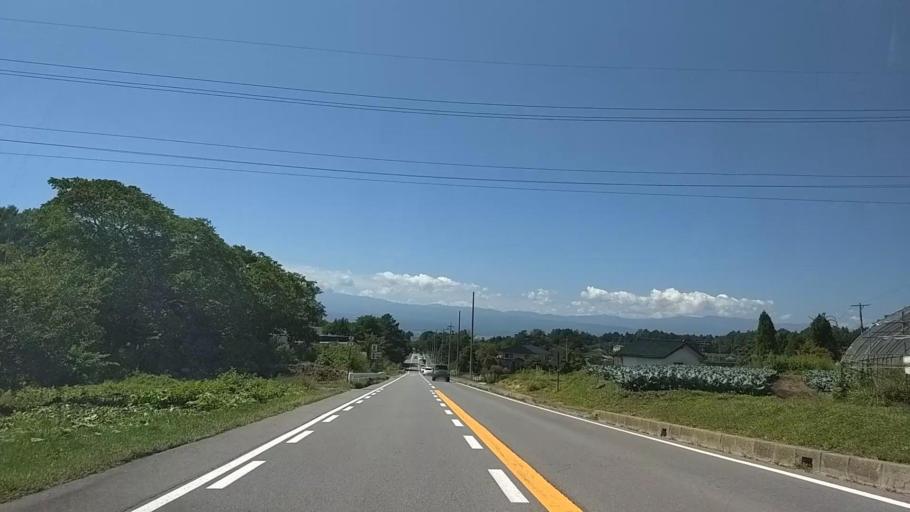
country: JP
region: Nagano
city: Komoro
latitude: 36.3412
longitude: 138.5212
